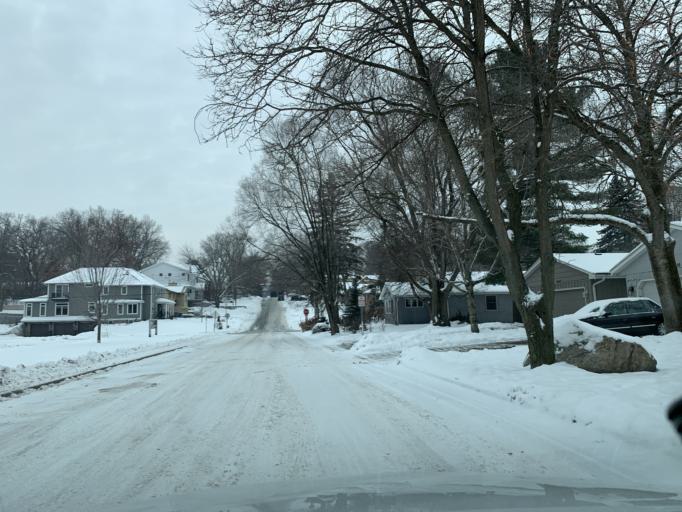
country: US
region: Minnesota
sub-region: Hennepin County
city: Edina
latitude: 44.9176
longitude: -93.3581
